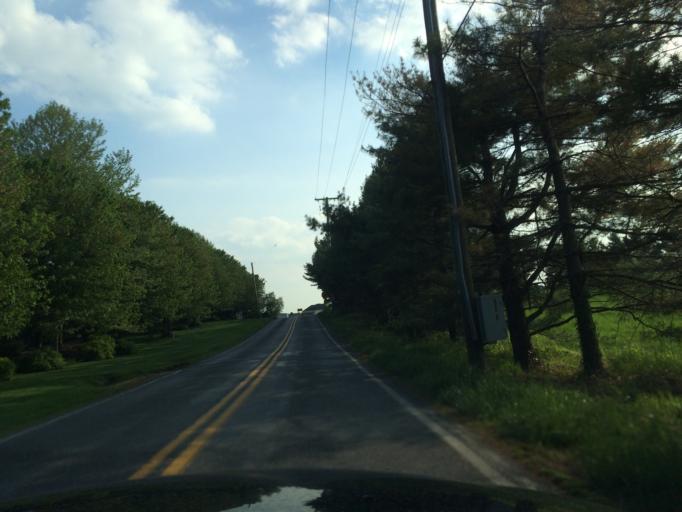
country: US
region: Maryland
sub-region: Carroll County
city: Sykesville
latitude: 39.2925
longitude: -77.0458
